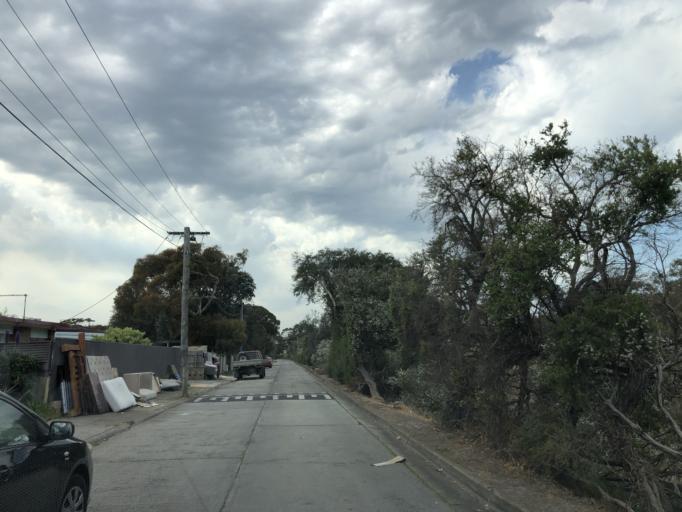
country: AU
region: Victoria
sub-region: Kingston
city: Carrum
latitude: -38.0821
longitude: 145.1289
